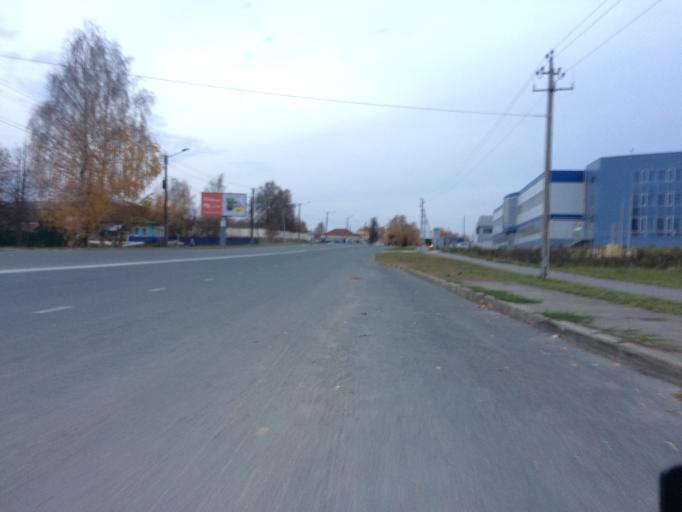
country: RU
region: Mariy-El
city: Yoshkar-Ola
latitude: 56.6048
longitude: 47.8813
